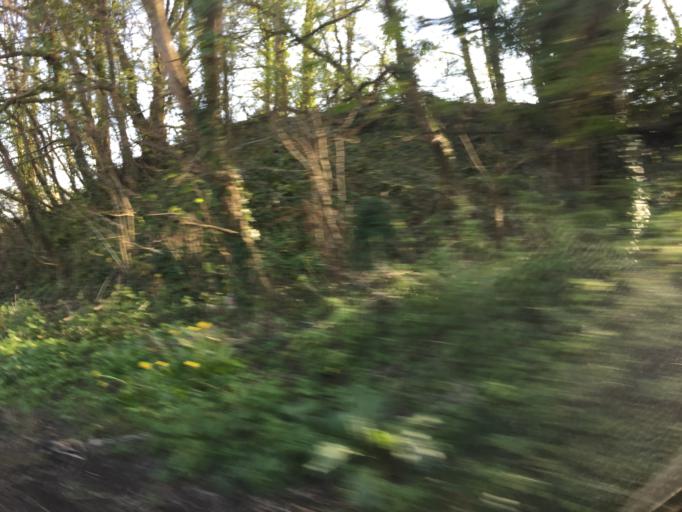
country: GB
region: Wales
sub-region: Monmouthshire
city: Usk
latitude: 51.7068
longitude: -2.9098
